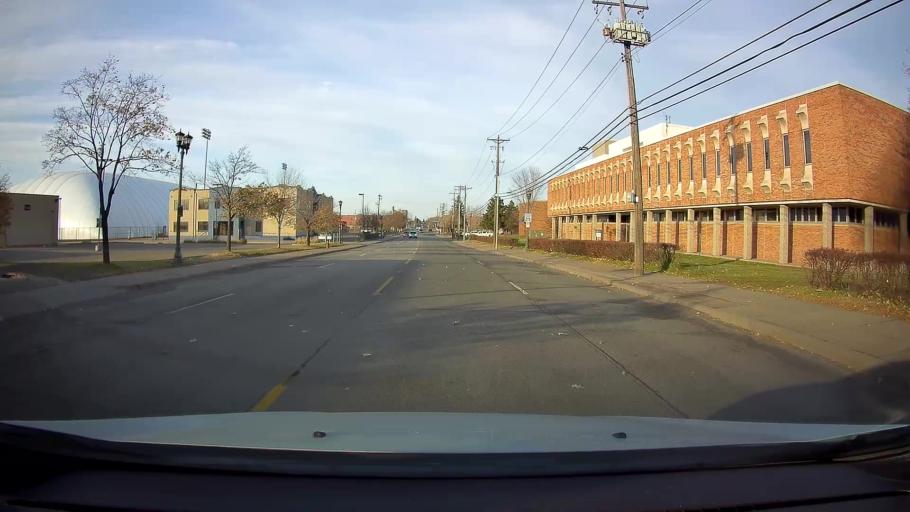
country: US
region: Minnesota
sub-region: Ramsey County
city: Falcon Heights
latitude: 44.9491
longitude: -93.1568
